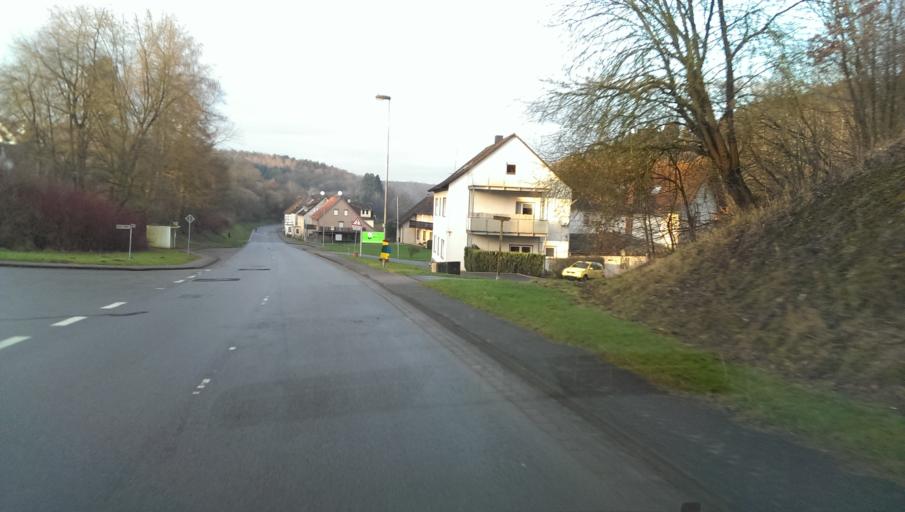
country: DE
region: Lower Saxony
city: Lenne
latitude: 51.8938
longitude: 9.6837
